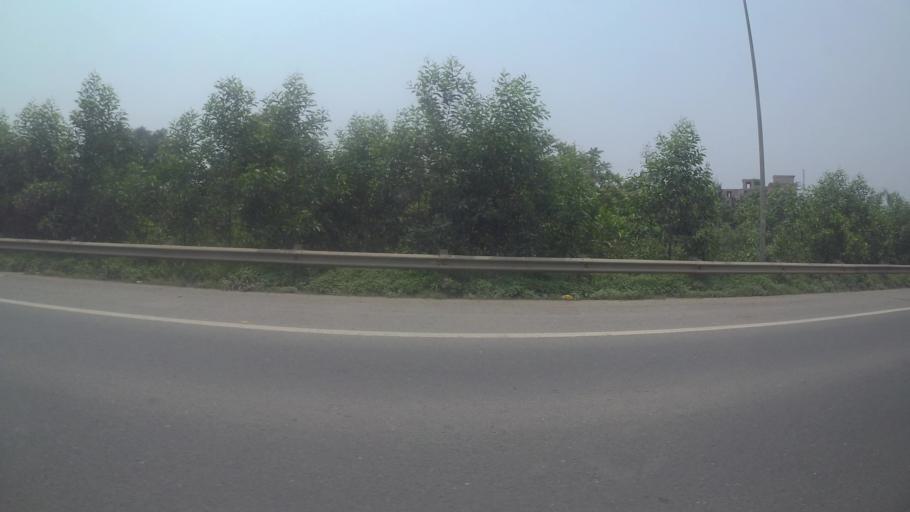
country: VN
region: Ha Noi
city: Lien Quan
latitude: 20.9897
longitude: 105.5586
